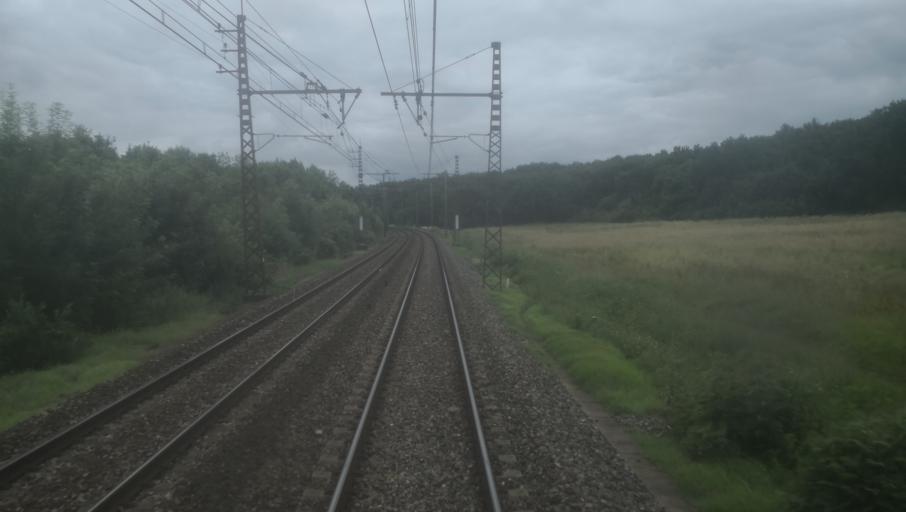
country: FR
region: Midi-Pyrenees
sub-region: Departement du Tarn-et-Garonne
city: Verdun-sur-Garonne
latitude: 43.8782
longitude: 1.2707
